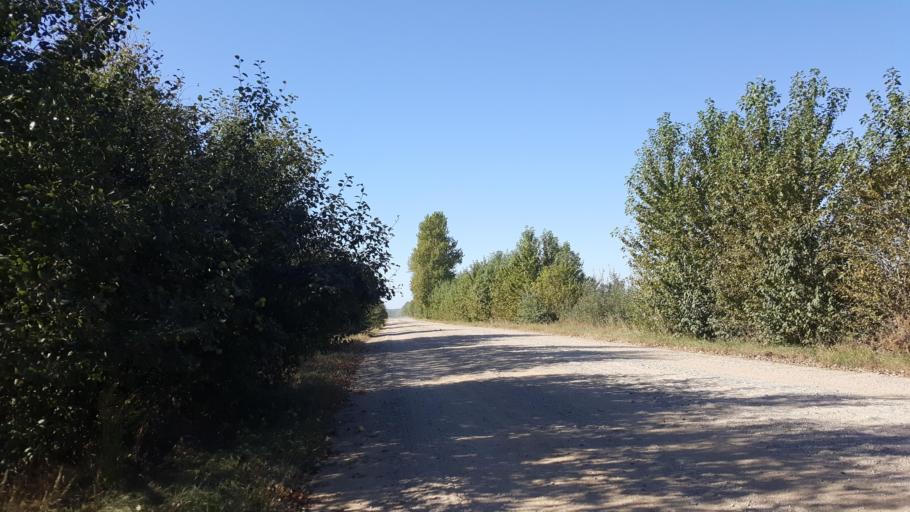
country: BY
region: Brest
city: Kamyanyets
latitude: 52.3549
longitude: 23.6939
